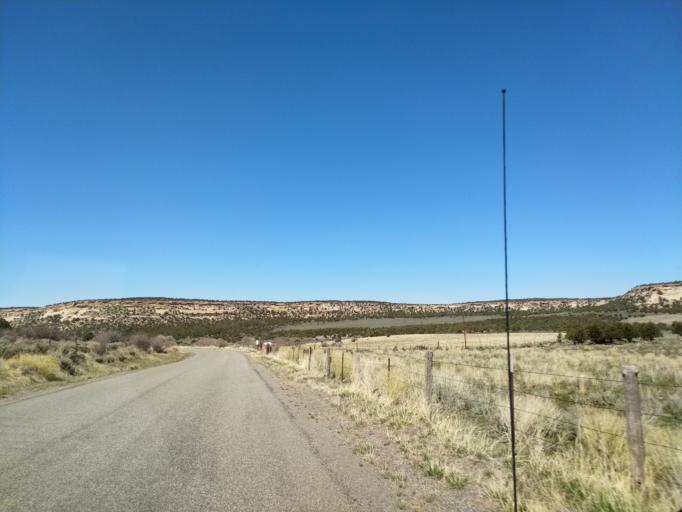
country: US
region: Colorado
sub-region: Mesa County
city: Loma
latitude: 38.9604
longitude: -109.0068
